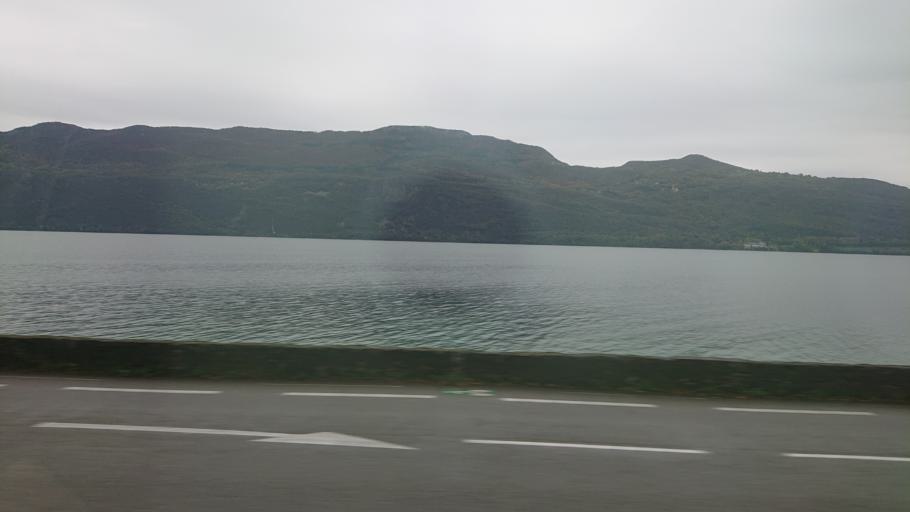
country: FR
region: Rhone-Alpes
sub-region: Departement de la Savoie
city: Brison-Saint-Innocent
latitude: 45.7516
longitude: 5.8810
